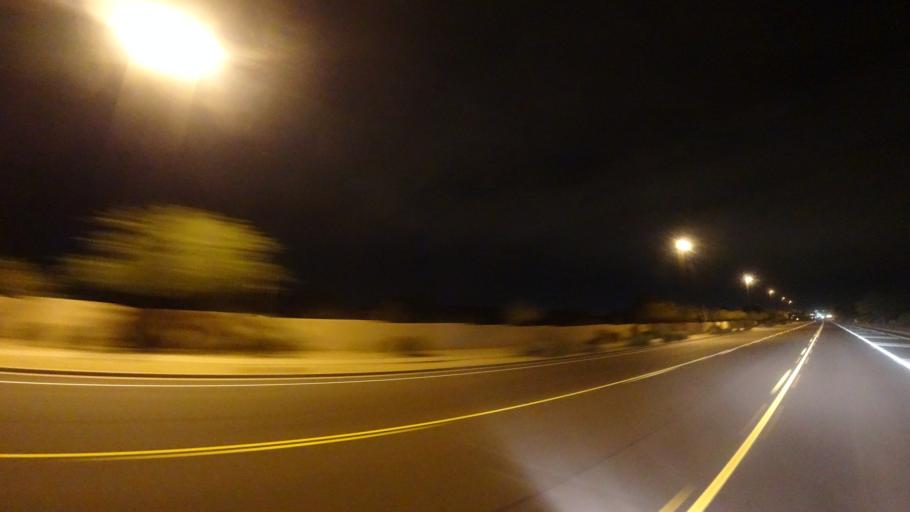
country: US
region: Arizona
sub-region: Pinal County
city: Apache Junction
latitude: 33.4661
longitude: -111.6424
